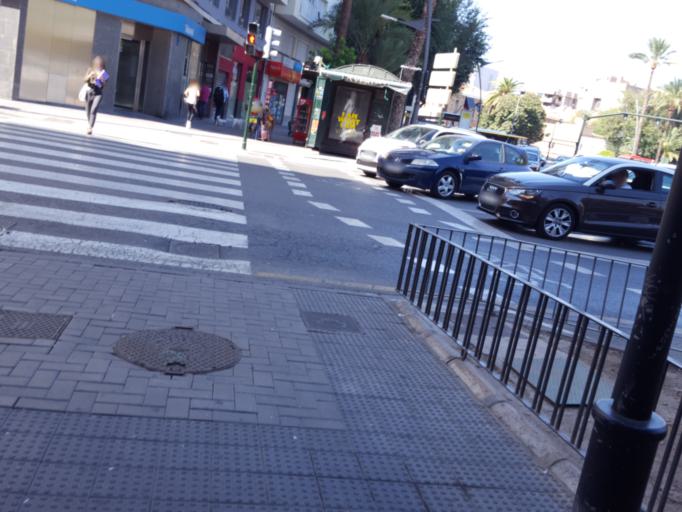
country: ES
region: Murcia
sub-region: Murcia
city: Murcia
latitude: 37.9914
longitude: -1.1307
